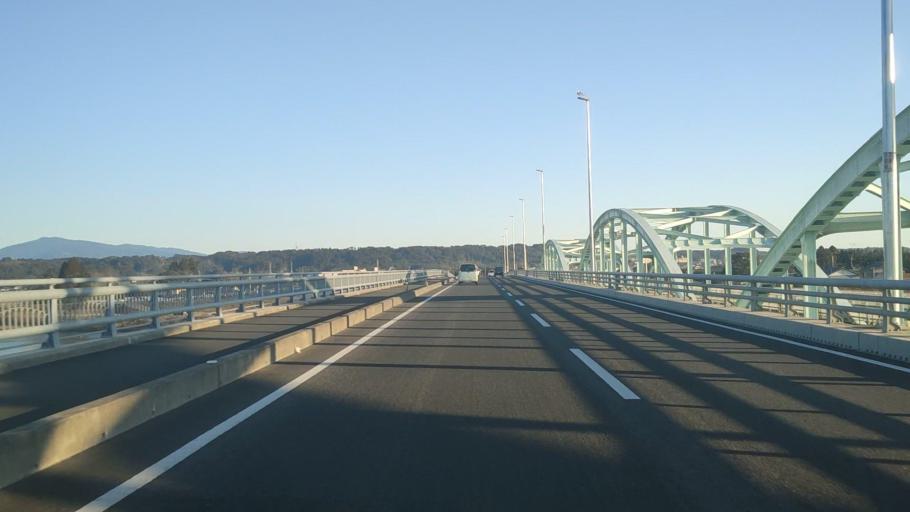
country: JP
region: Miyazaki
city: Takanabe
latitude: 32.0499
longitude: 131.4725
